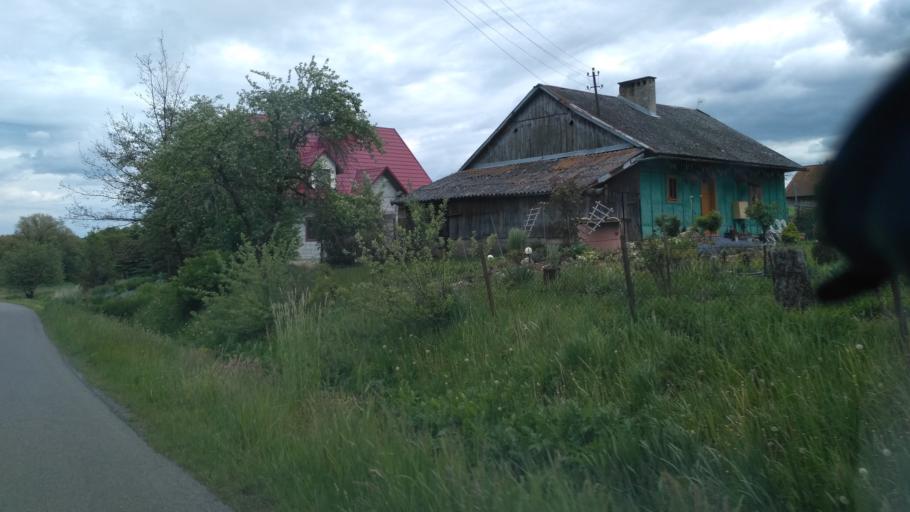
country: PL
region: Subcarpathian Voivodeship
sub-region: Powiat przeworski
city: Jawornik Polski
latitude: 49.8348
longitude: 22.3054
